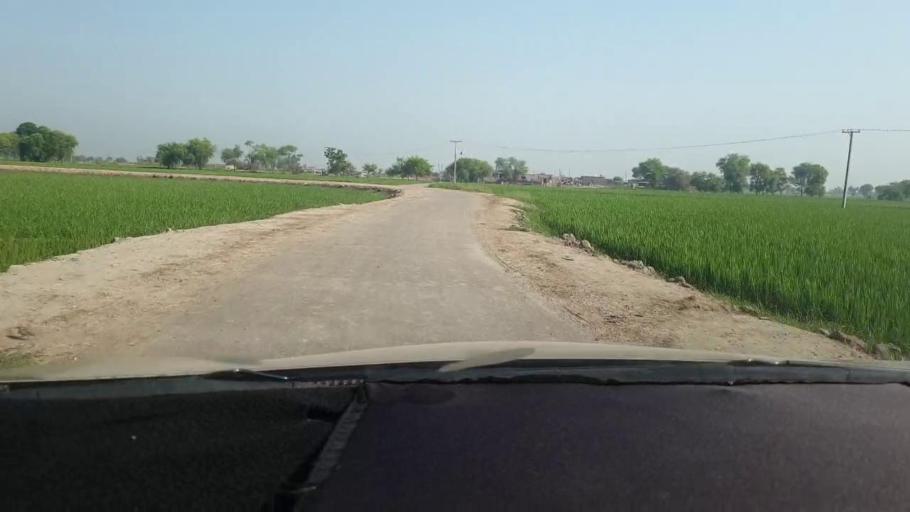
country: PK
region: Sindh
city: Miro Khan
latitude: 27.7541
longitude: 68.1482
